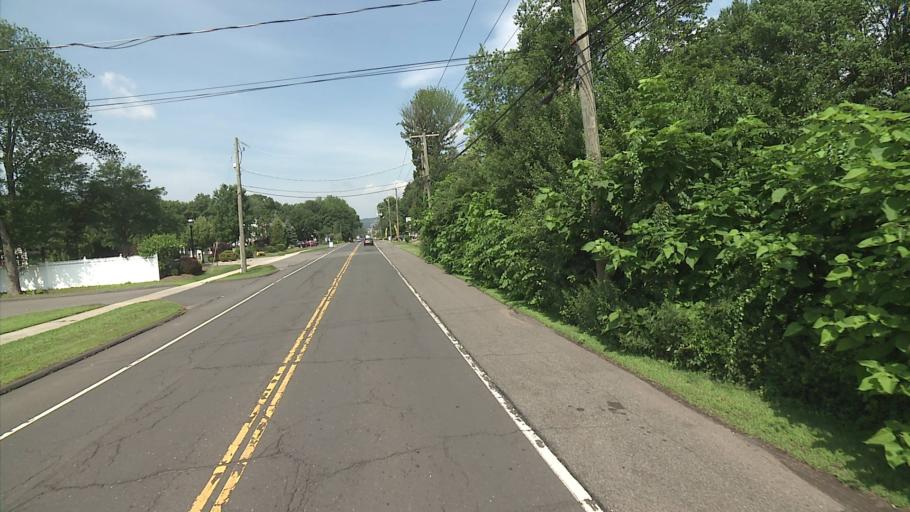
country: US
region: Connecticut
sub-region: New Haven County
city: Cheshire Village
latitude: 41.5647
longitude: -72.8936
